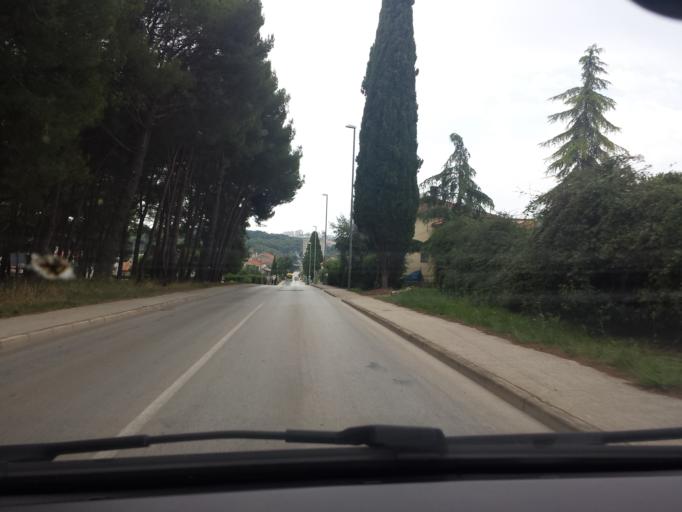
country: HR
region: Istarska
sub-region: Grad Pula
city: Pula
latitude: 44.8935
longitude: 13.8504
